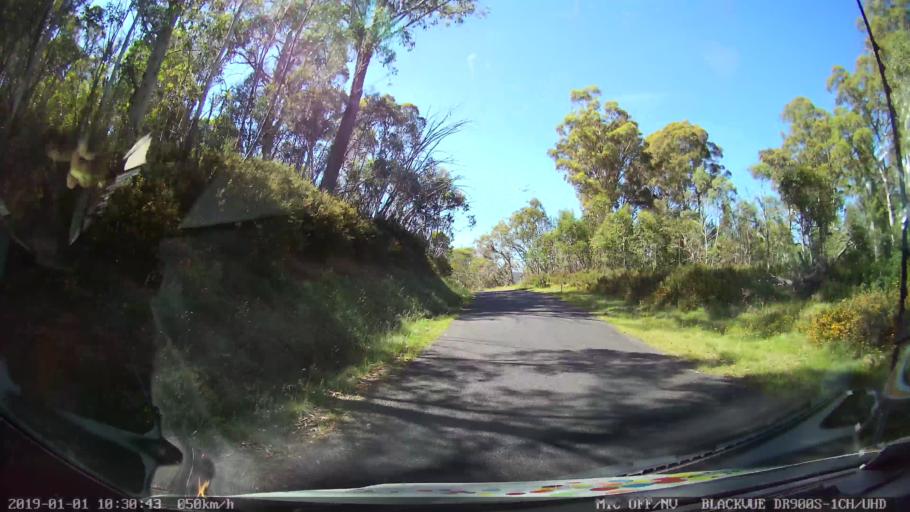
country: AU
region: New South Wales
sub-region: Snowy River
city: Jindabyne
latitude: -36.0529
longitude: 148.2605
